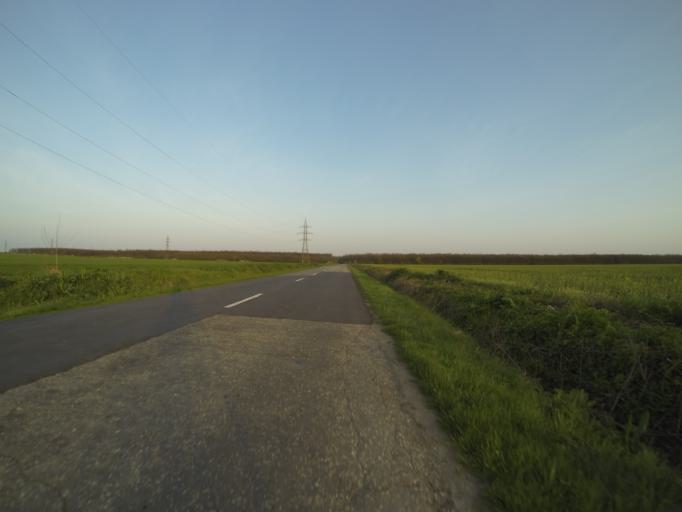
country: RO
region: Dolj
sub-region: Comuna Dranicu
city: Dranic
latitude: 44.0695
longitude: 23.7997
